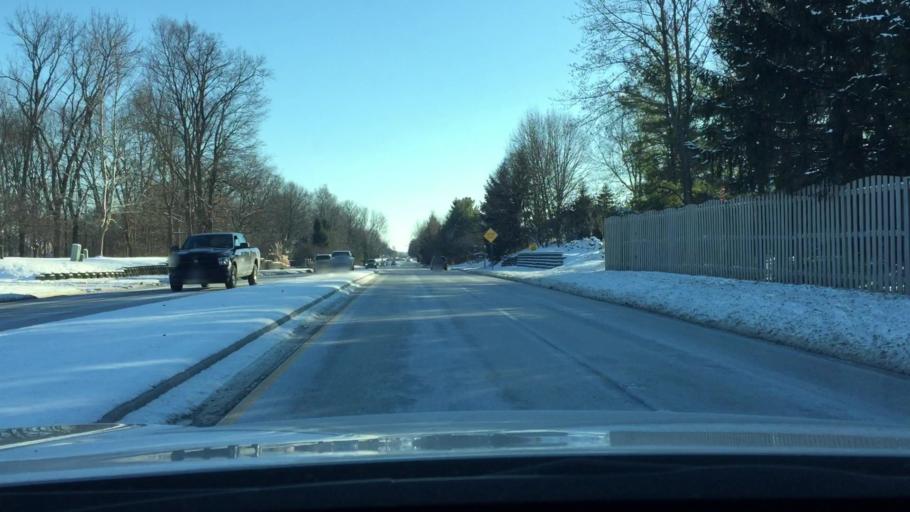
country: US
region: Indiana
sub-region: Hamilton County
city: Carmel
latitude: 39.9973
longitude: -86.0706
